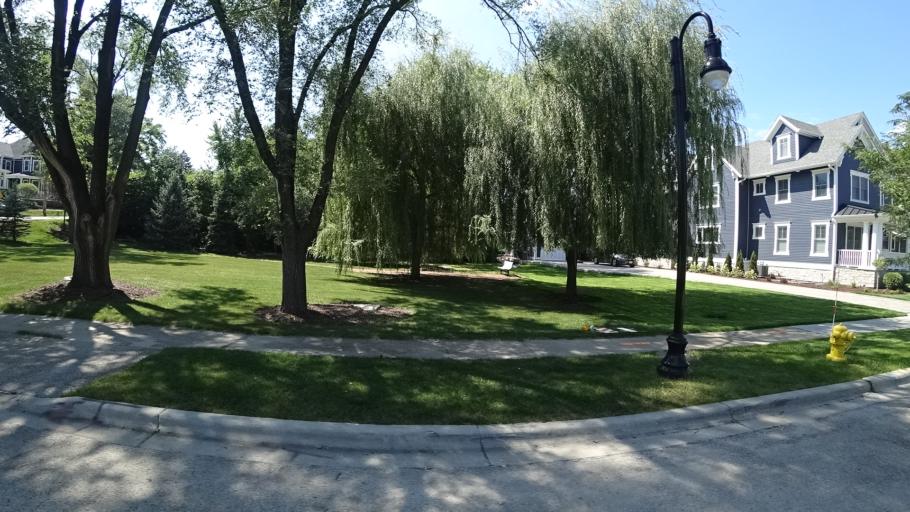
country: US
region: Illinois
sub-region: Cook County
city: Orland Park
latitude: 41.6281
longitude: -87.8613
